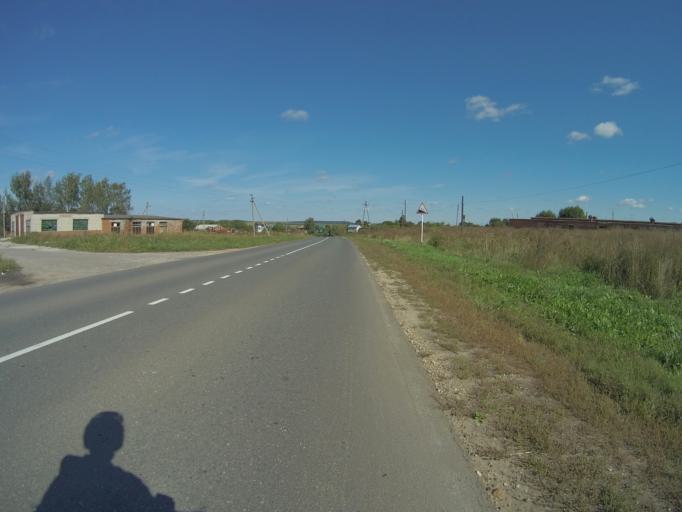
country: RU
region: Vladimir
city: Bogolyubovo
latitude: 56.2659
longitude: 40.4791
